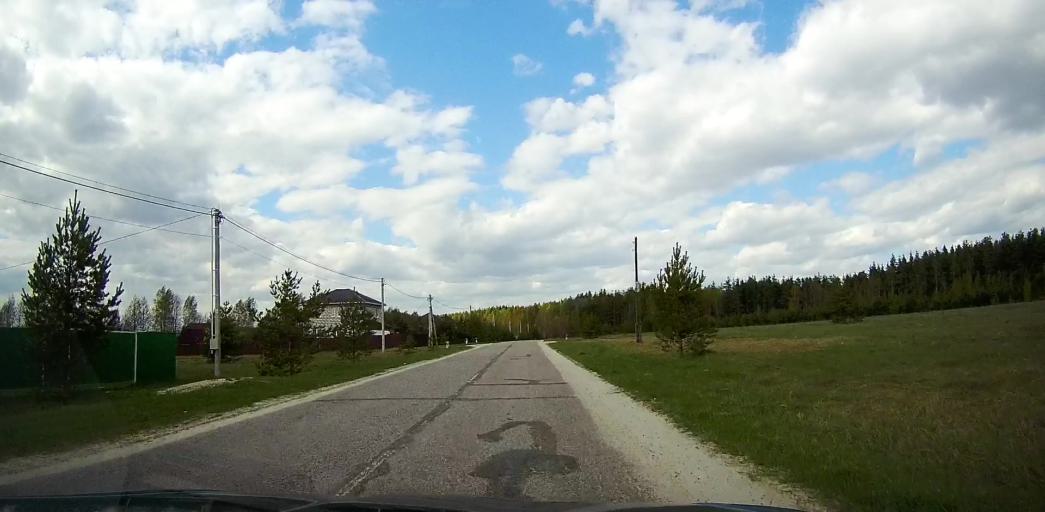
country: RU
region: Moskovskaya
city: Davydovo
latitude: 55.6412
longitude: 38.7758
